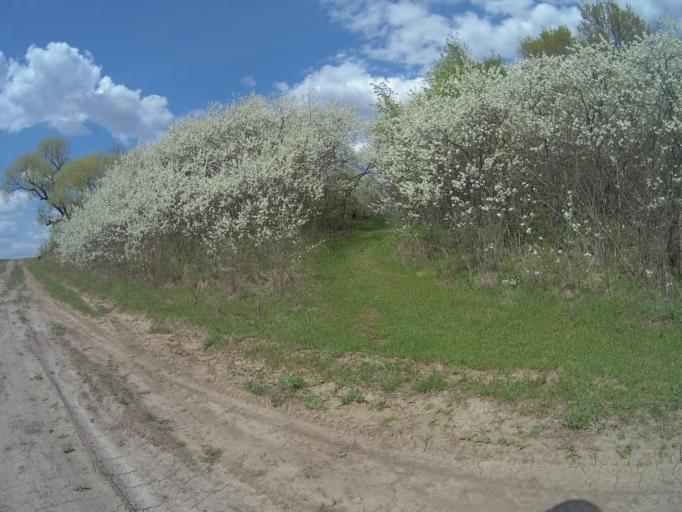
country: RU
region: Vladimir
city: Suzdal'
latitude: 56.3312
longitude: 40.3623
